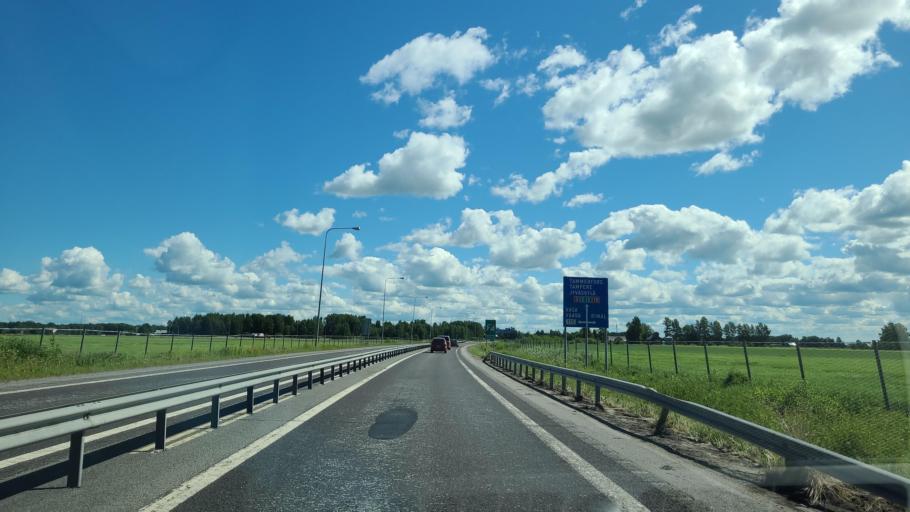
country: FI
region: Ostrobothnia
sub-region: Vaasa
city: Ristinummi
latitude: 63.0250
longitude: 21.7829
